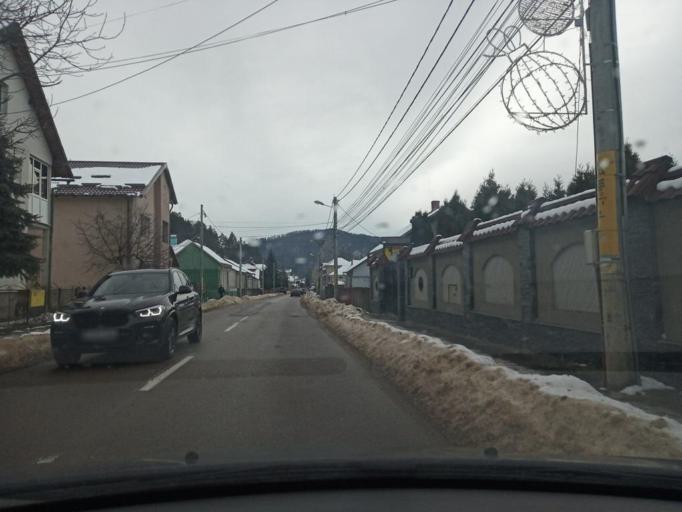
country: RO
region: Suceava
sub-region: Oras Gura Humorului
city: Gura Humorului
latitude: 47.5610
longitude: 25.8868
